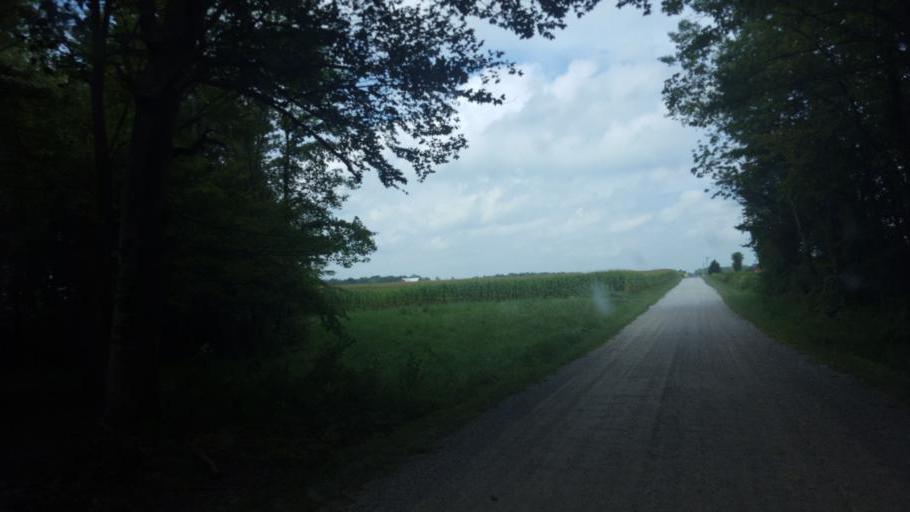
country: US
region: Ohio
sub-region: Morrow County
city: Mount Gilead
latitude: 40.6177
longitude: -82.7091
